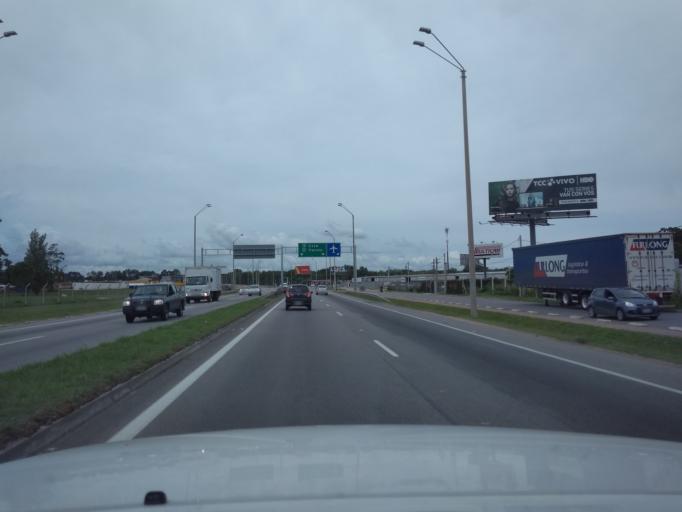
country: UY
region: Canelones
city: Barra de Carrasco
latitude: -34.8443
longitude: -56.0191
